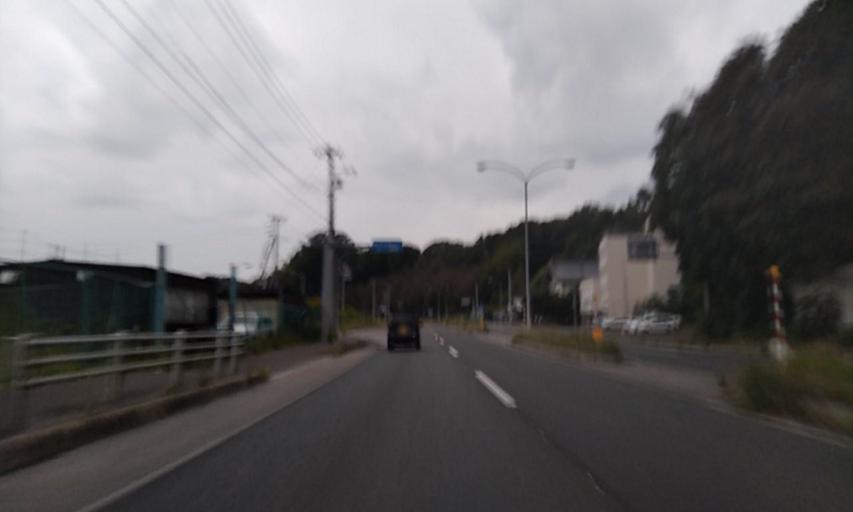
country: JP
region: Hokkaido
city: Abashiri
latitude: 44.0173
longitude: 144.2836
